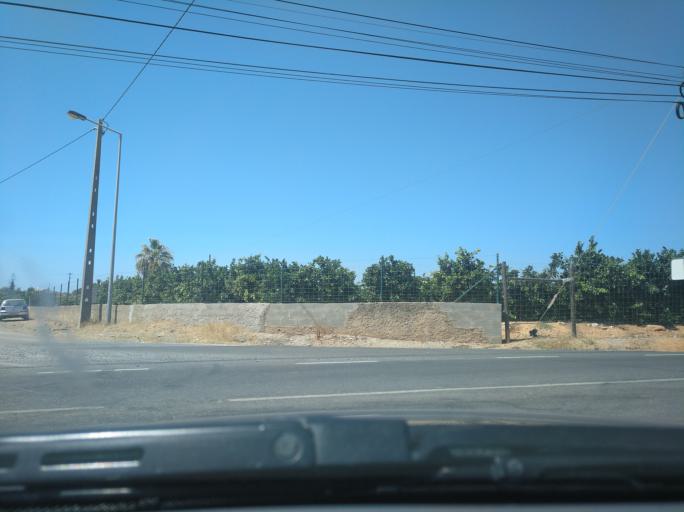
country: PT
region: Faro
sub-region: Faro
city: Faro
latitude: 37.0309
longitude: -7.8972
